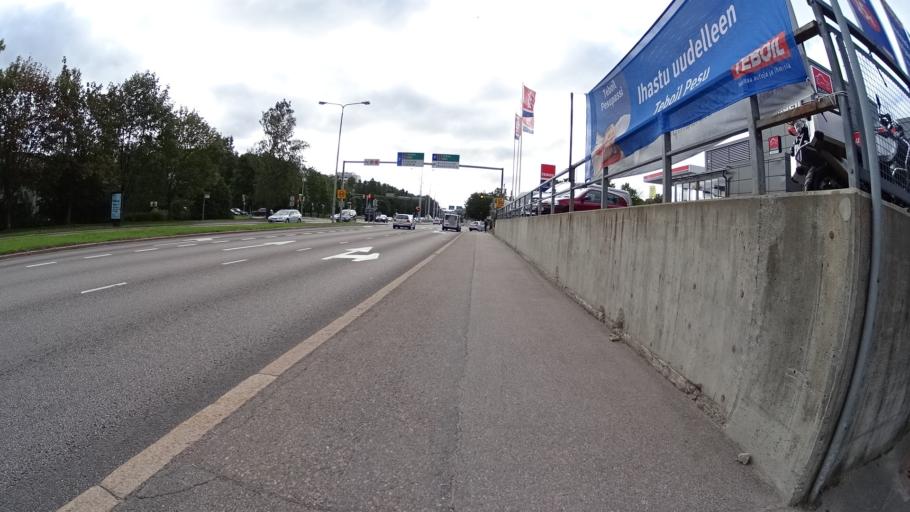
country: FI
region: Uusimaa
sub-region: Helsinki
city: Teekkarikylae
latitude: 60.2073
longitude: 24.8794
